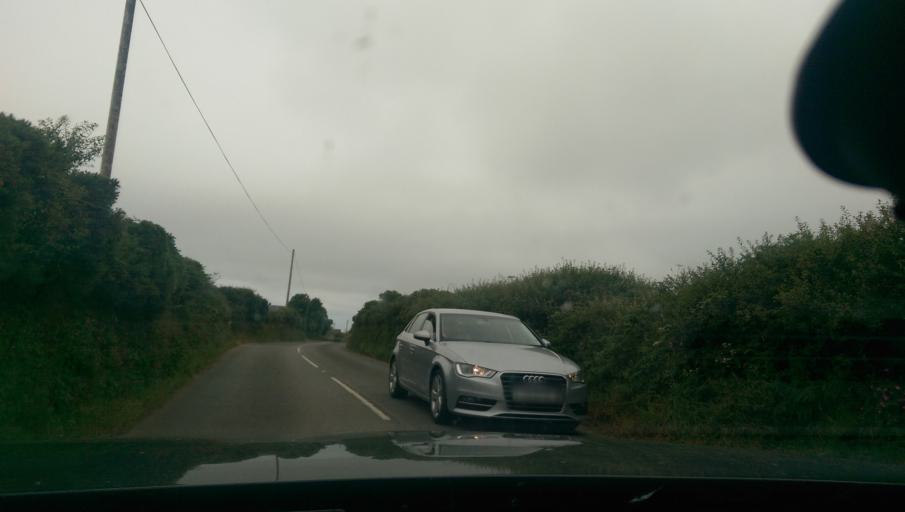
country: GB
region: England
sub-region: Cornwall
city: Saint Just
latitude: 50.1096
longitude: -5.6750
